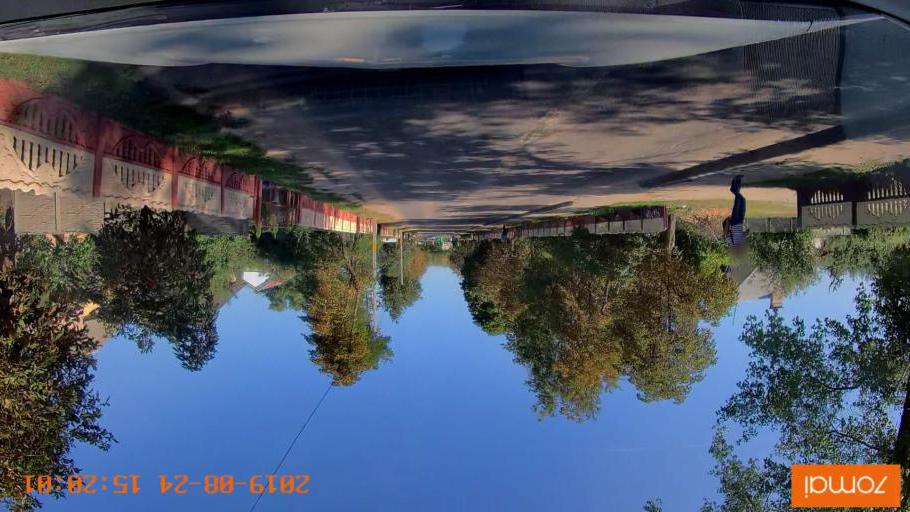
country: BY
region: Minsk
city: Samakhvalavichy
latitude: 53.6784
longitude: 27.5296
